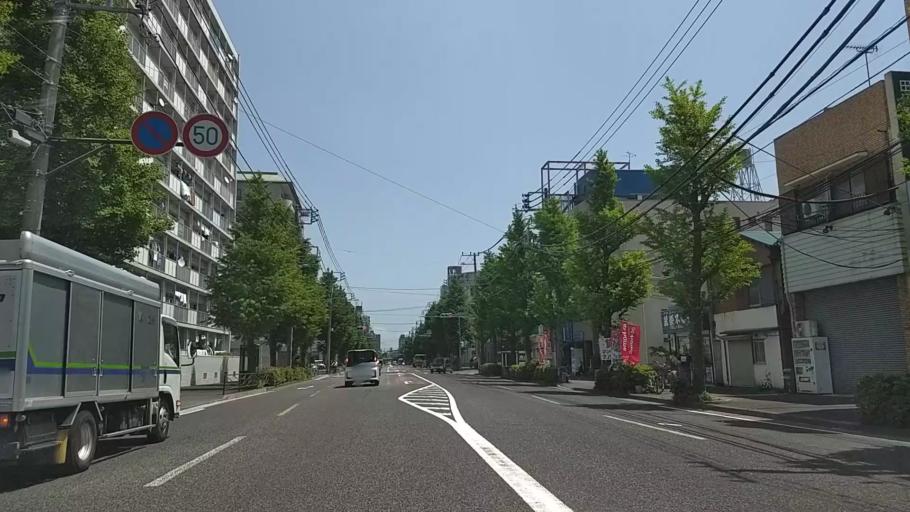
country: JP
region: Kanagawa
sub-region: Kawasaki-shi
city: Kawasaki
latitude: 35.5251
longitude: 139.7170
